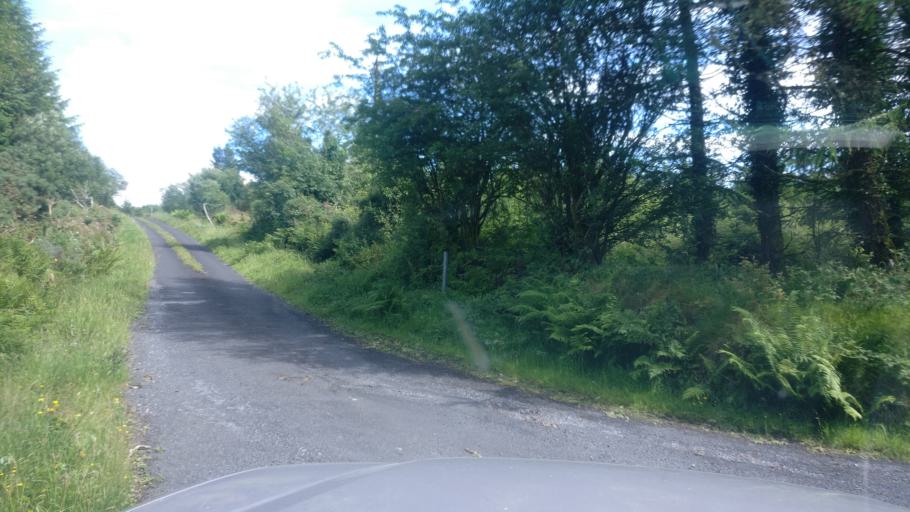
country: IE
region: Connaught
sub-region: County Galway
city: Gort
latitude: 53.0641
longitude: -8.6978
